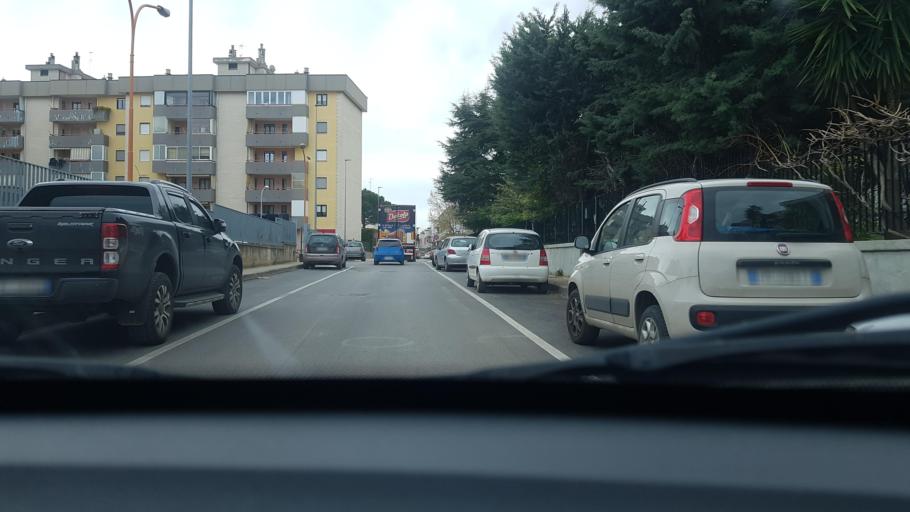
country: IT
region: Apulia
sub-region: Provincia di Bari
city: Noicattaro
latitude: 41.0344
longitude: 16.9827
